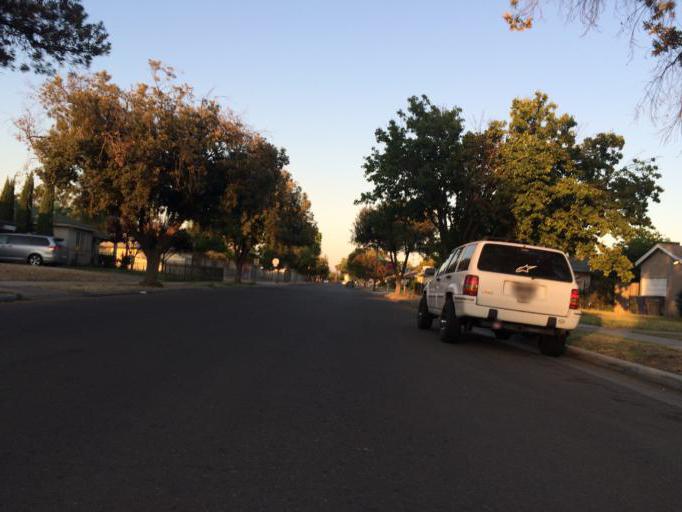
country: US
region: California
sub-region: Fresno County
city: Fresno
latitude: 36.7759
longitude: -119.7756
